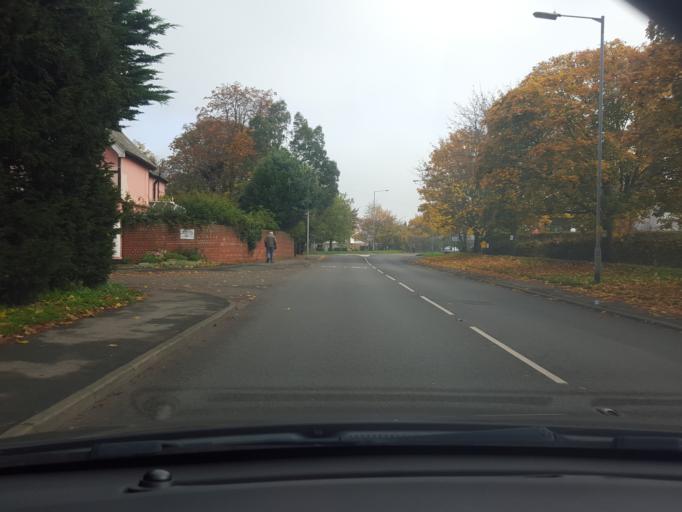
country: GB
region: England
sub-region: Essex
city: Manningtree
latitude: 51.9383
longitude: 1.0440
